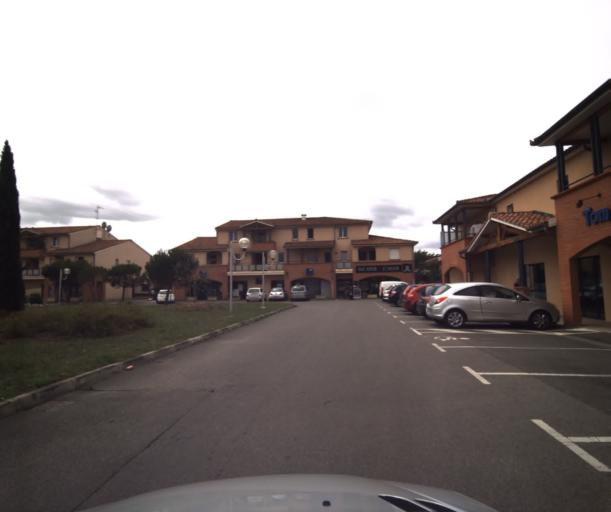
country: FR
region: Midi-Pyrenees
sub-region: Departement de la Haute-Garonne
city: Pinsaguel
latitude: 43.5021
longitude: 1.3917
